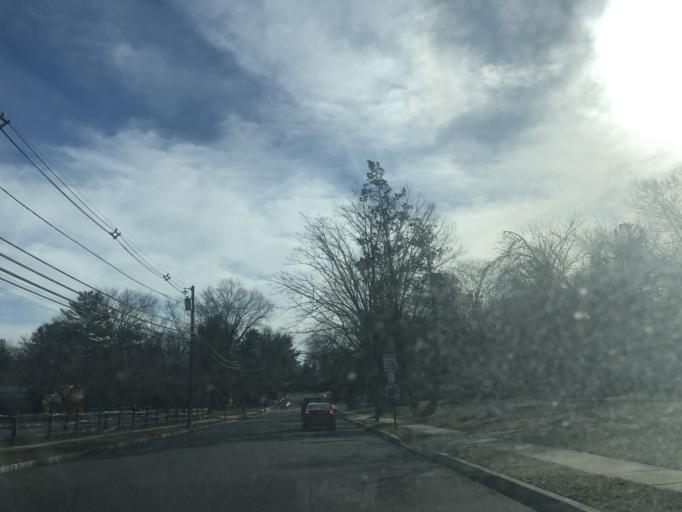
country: US
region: New Jersey
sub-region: Mercer County
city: Princeton
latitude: 40.3545
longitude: -74.6378
